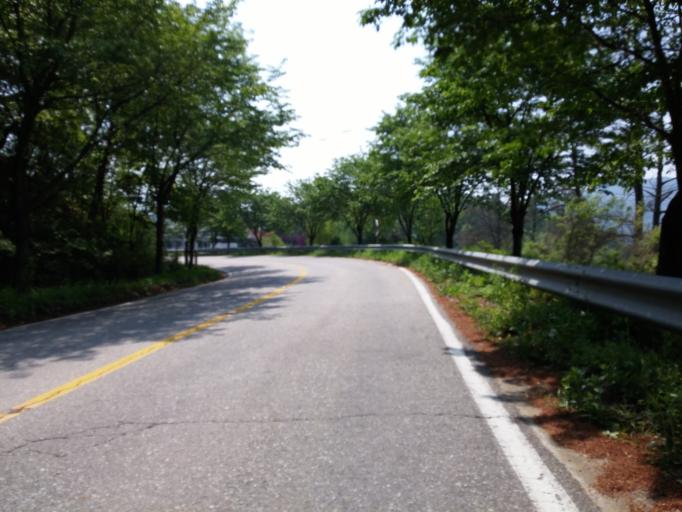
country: KR
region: Chungcheongbuk-do
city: Okcheon
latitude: 36.4343
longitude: 127.5636
